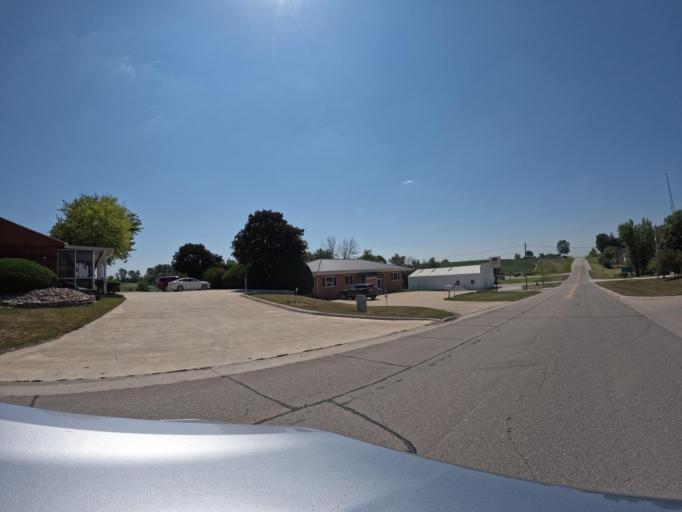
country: US
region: Iowa
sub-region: Keokuk County
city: Sigourney
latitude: 41.3226
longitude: -92.2052
